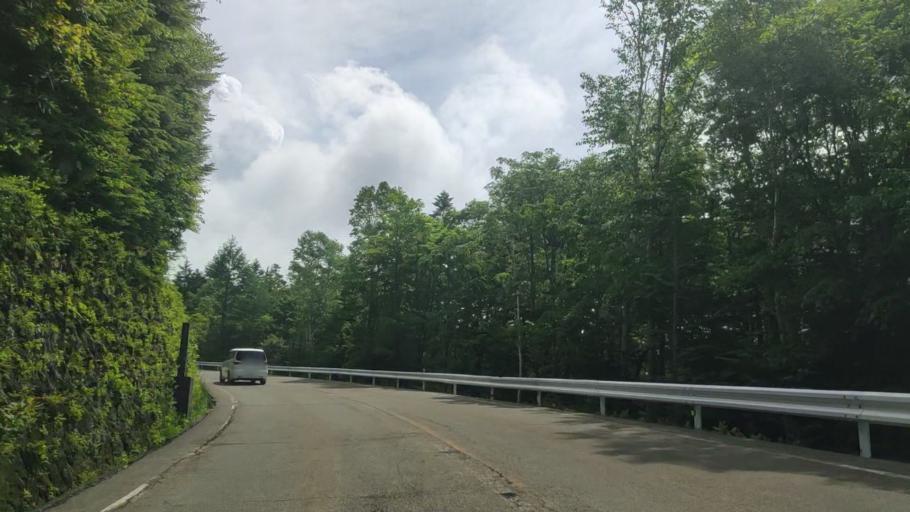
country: JP
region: Yamanashi
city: Fujikawaguchiko
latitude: 35.4053
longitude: 138.6992
